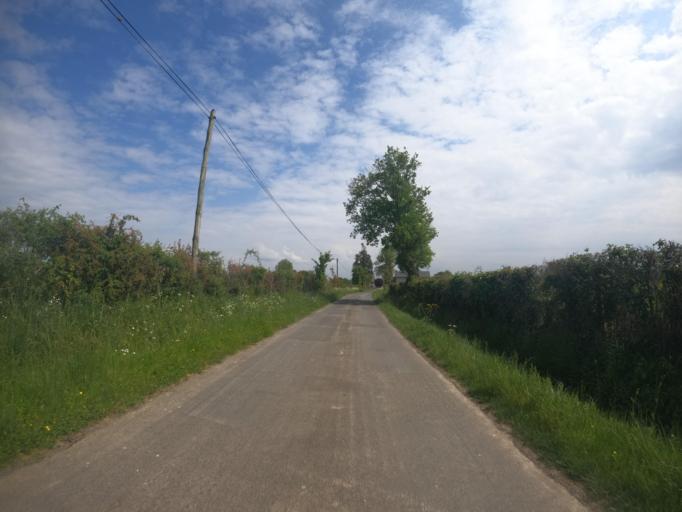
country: FR
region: Poitou-Charentes
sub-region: Departement des Deux-Sevres
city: Saint-Varent
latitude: 46.8929
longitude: -0.2826
